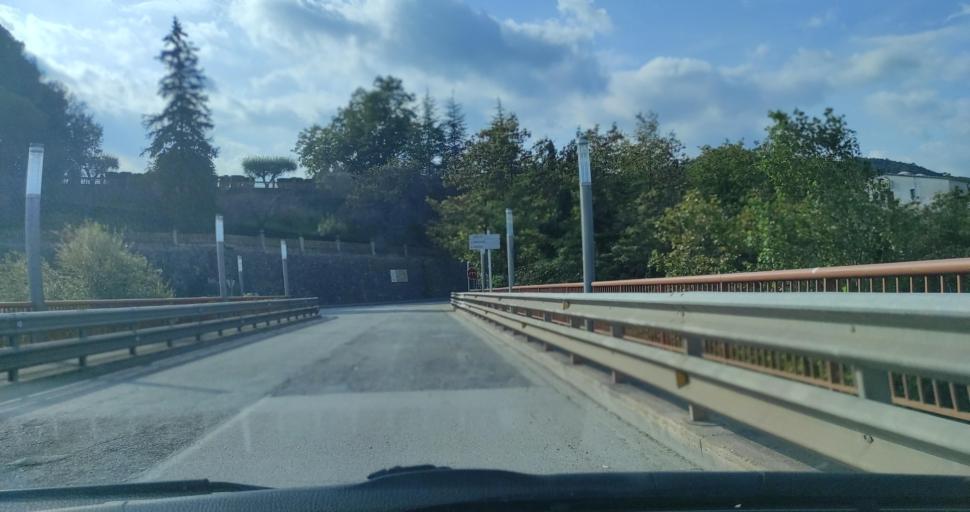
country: ES
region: Catalonia
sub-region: Provincia de Girona
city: Besalu
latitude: 42.2010
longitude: 2.6991
